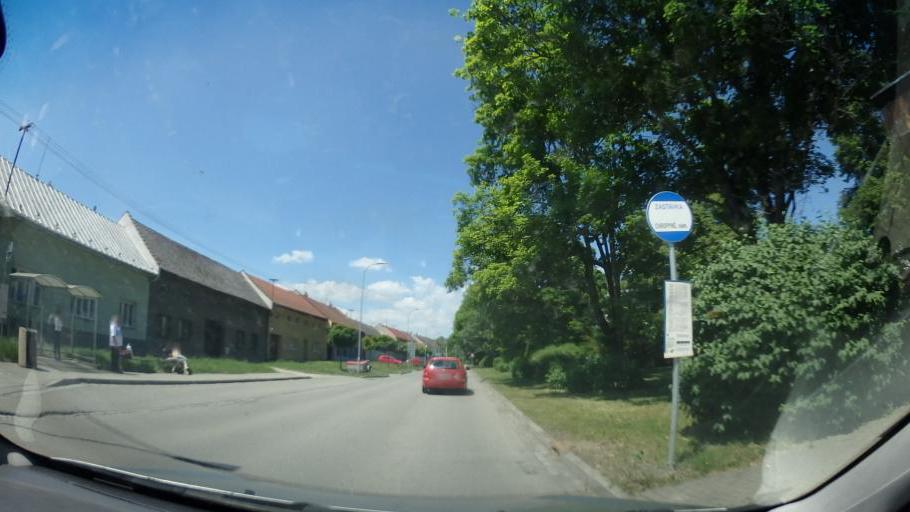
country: CZ
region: Zlin
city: Chropyne
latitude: 49.3578
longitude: 17.3623
